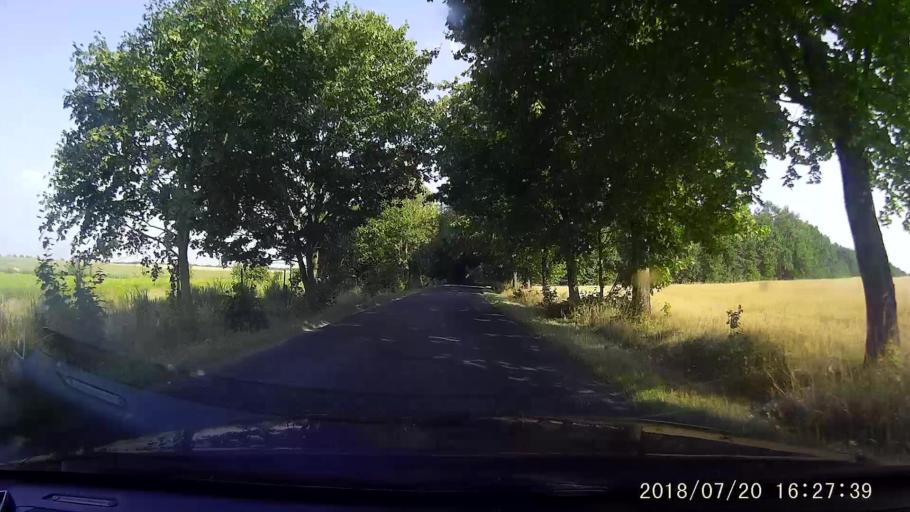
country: PL
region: Lower Silesian Voivodeship
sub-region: Powiat zgorzelecki
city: Lagow
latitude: 51.1245
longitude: 15.0478
